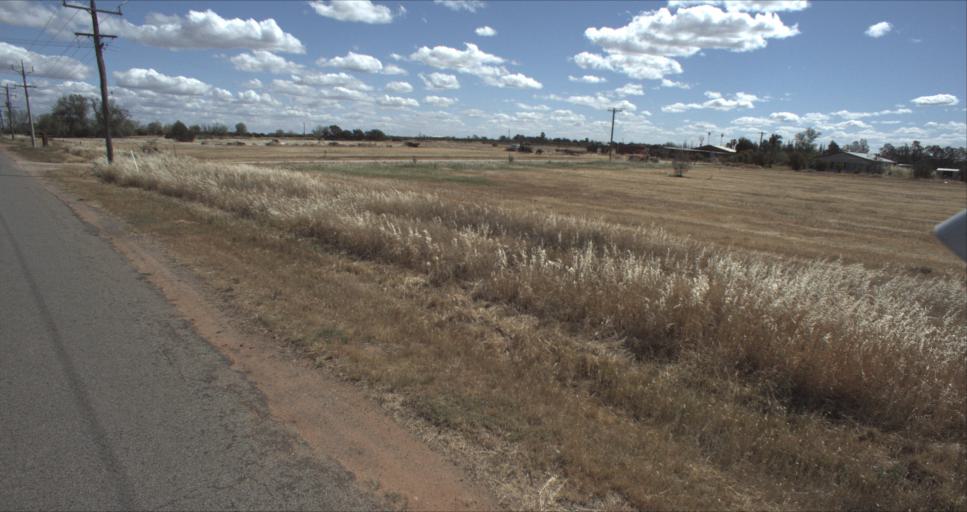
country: AU
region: New South Wales
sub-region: Leeton
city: Leeton
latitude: -34.5131
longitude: 146.2519
